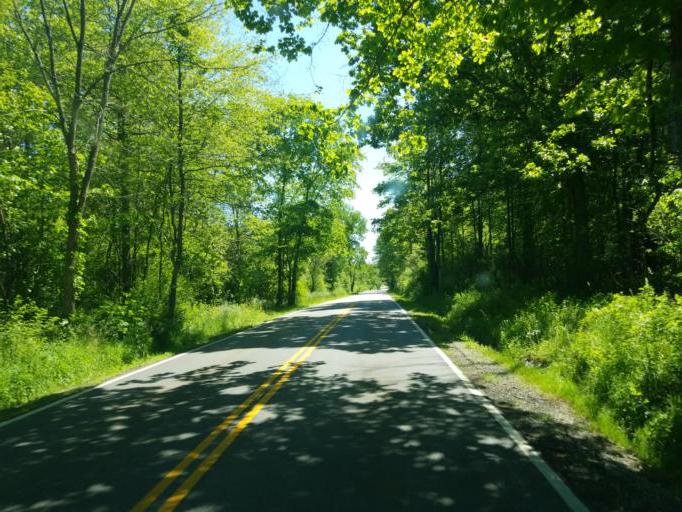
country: US
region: Ohio
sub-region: Portage County
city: Aurora
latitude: 41.2856
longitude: -81.3886
